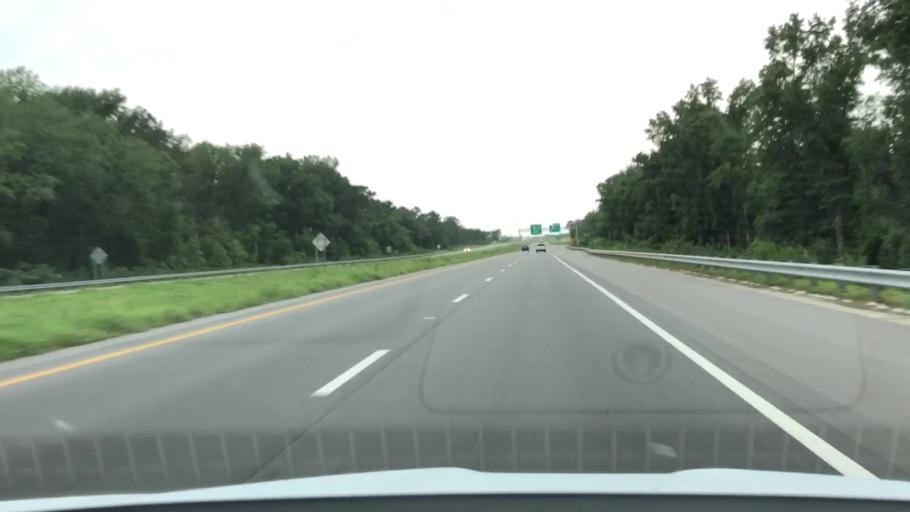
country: US
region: North Carolina
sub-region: Lenoir County
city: La Grange
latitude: 35.2974
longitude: -77.8088
